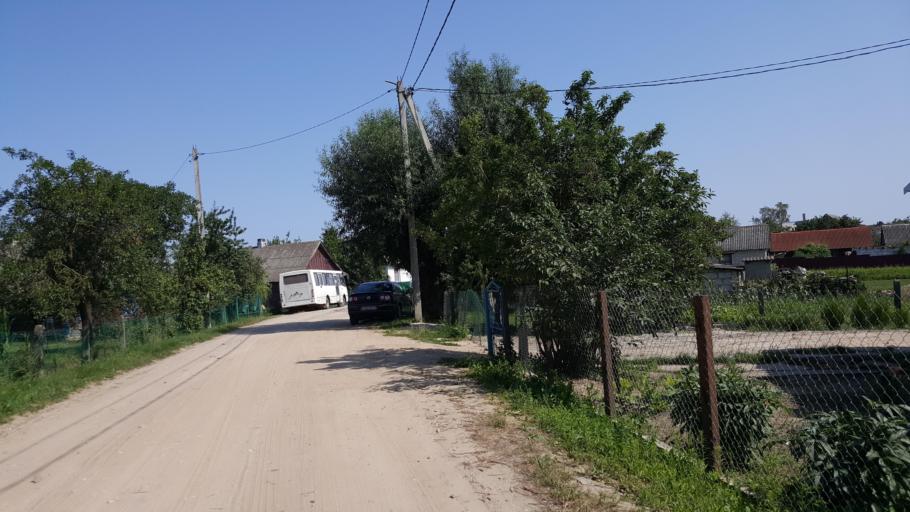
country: BY
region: Brest
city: Zhabinka
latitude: 52.2076
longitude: 23.9950
